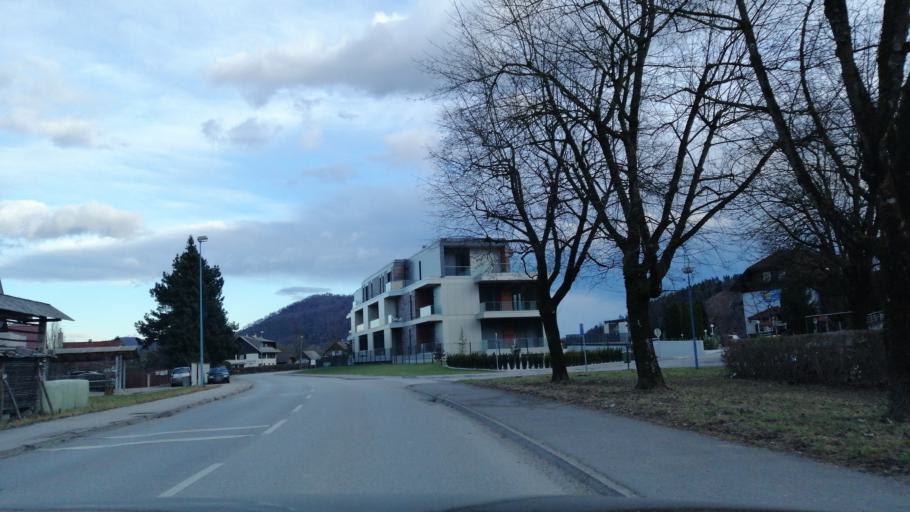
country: SI
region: Medvode
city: Medvode
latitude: 46.1340
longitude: 14.4146
